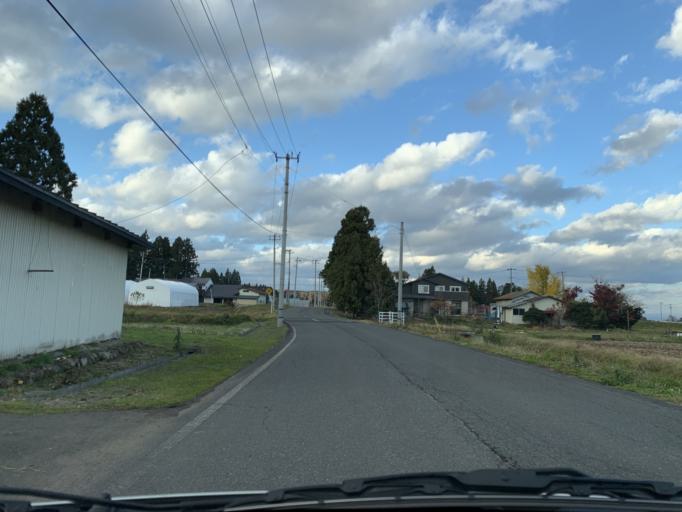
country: JP
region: Iwate
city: Mizusawa
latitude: 39.1110
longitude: 141.0237
